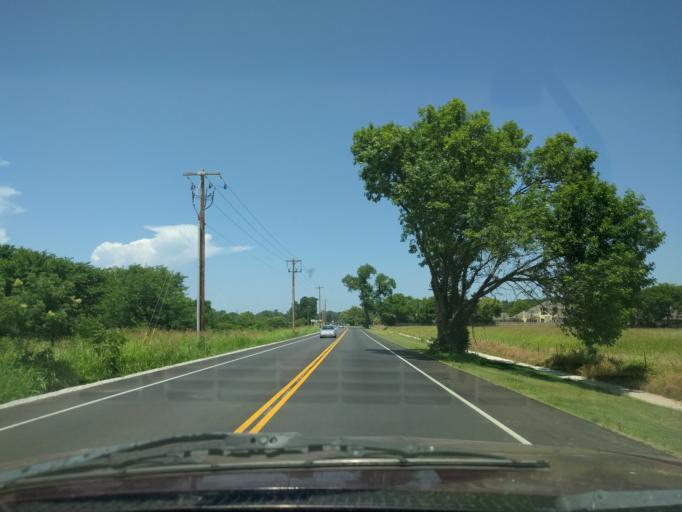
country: US
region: Oklahoma
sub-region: Tulsa County
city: Jenks
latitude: 35.9956
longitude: -95.9363
